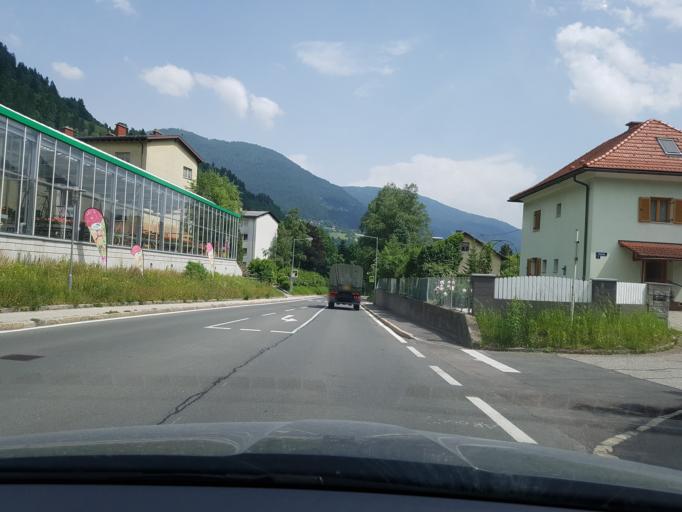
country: AT
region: Carinthia
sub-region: Politischer Bezirk Spittal an der Drau
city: Radenthein
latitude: 46.8007
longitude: 13.7115
